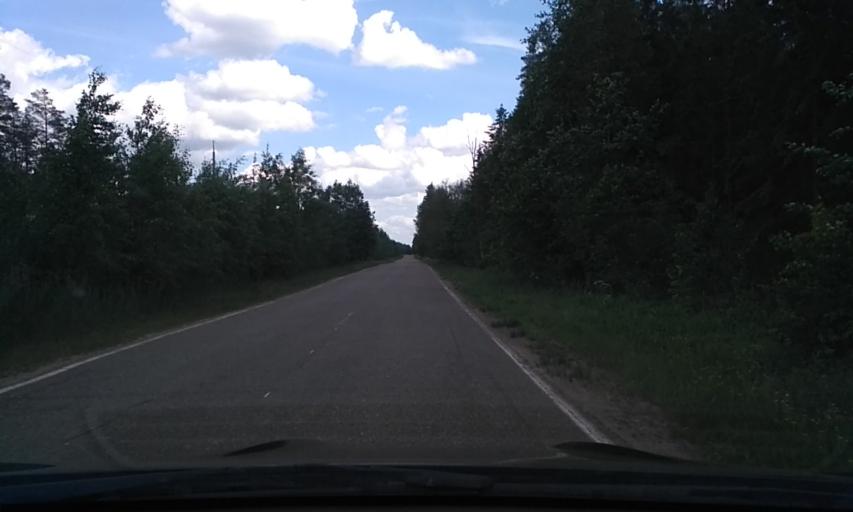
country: RU
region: Leningrad
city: Otradnoye
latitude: 59.8197
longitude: 30.8135
